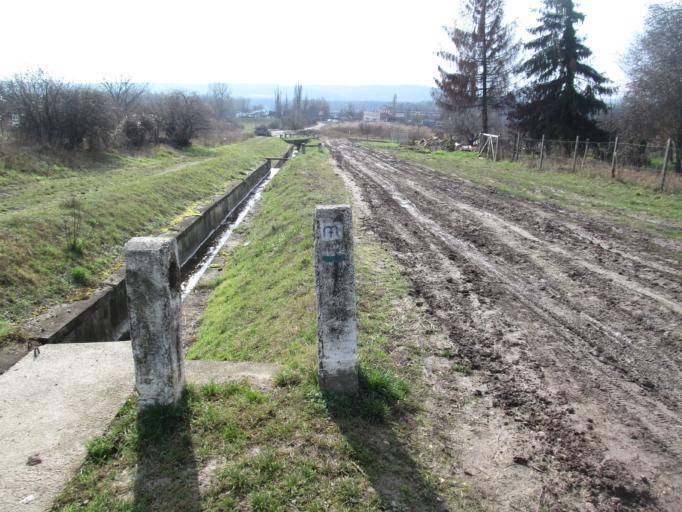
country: HU
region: Budapest
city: Budapest XII. keruelet
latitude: 47.4653
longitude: 18.9934
